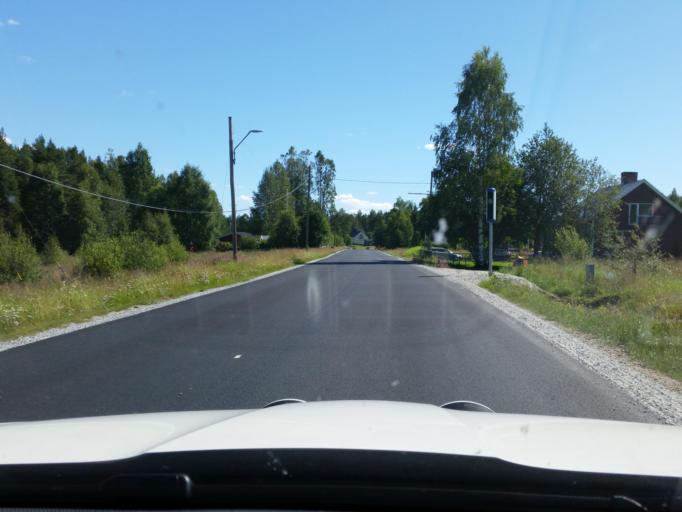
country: SE
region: Norrbotten
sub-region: Pitea Kommun
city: Roknas
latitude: 65.3446
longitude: 21.1276
